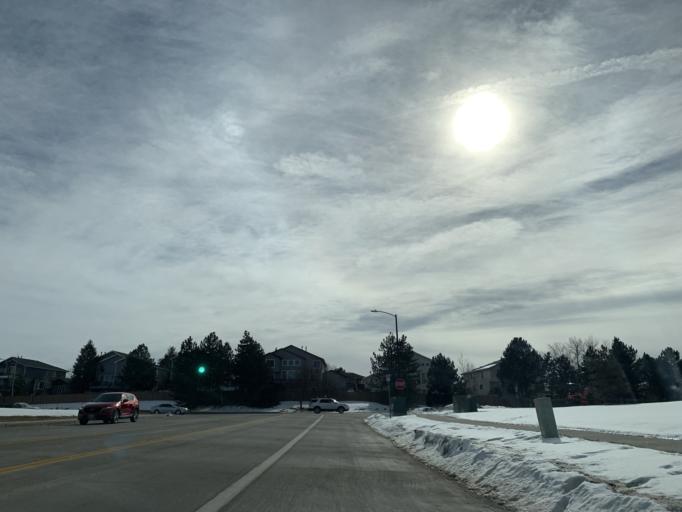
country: US
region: Colorado
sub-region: Douglas County
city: Carriage Club
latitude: 39.5411
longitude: -104.9156
